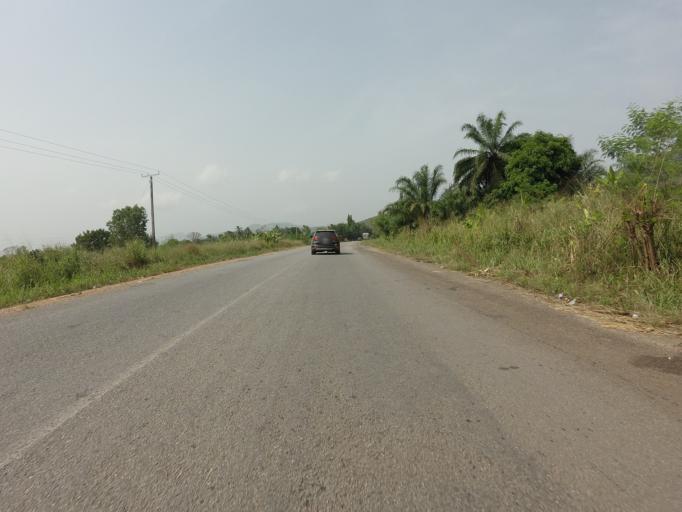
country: GH
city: Akropong
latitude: 6.2414
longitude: 0.1130
